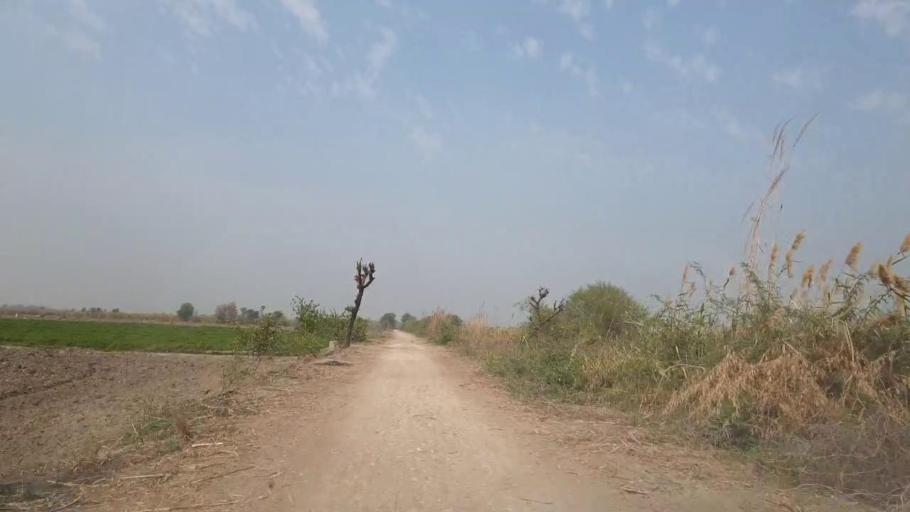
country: PK
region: Sindh
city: Mirpur Khas
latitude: 25.5625
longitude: 69.1062
